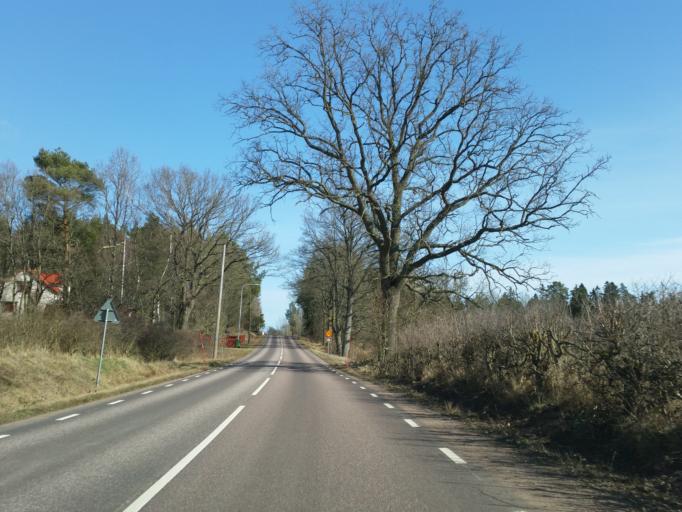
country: SE
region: Kalmar
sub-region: Monsteras Kommun
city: Timmernabben
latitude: 56.8580
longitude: 16.4033
